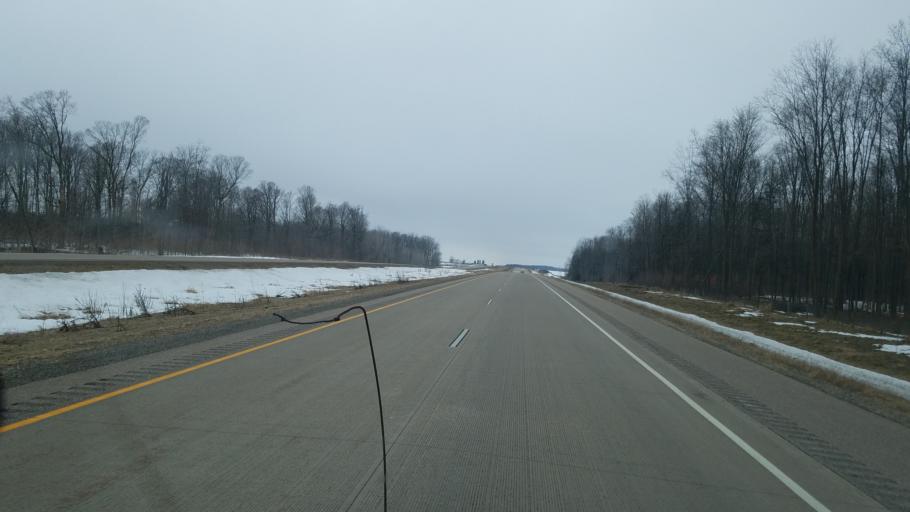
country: US
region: Wisconsin
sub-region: Wood County
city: Wisconsin Rapids
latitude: 44.6204
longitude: -89.8906
